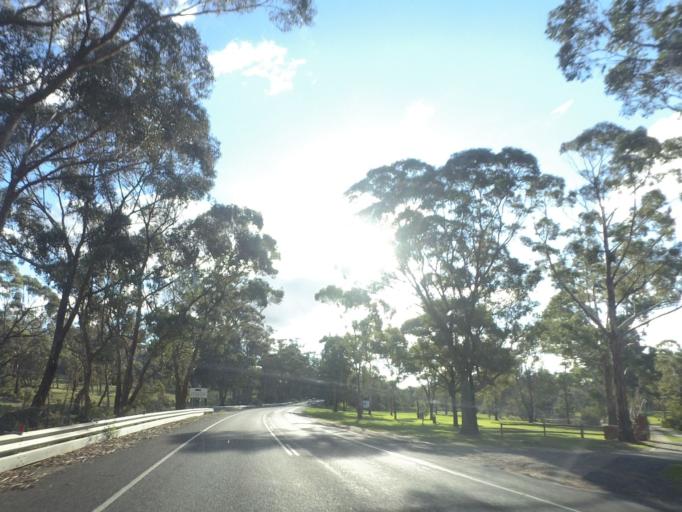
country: AU
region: Victoria
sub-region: Mount Alexander
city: Castlemaine
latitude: -37.0882
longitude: 144.2811
